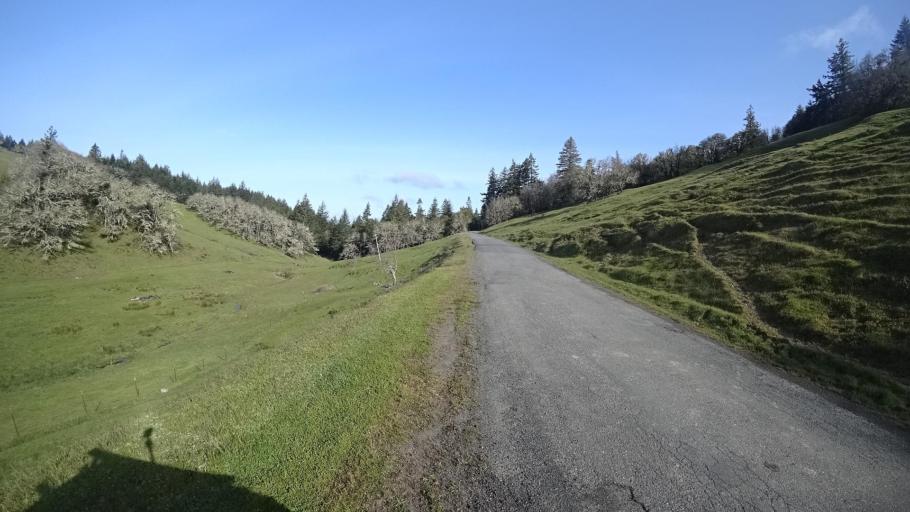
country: US
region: California
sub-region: Humboldt County
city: Hydesville
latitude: 40.6459
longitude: -123.9214
